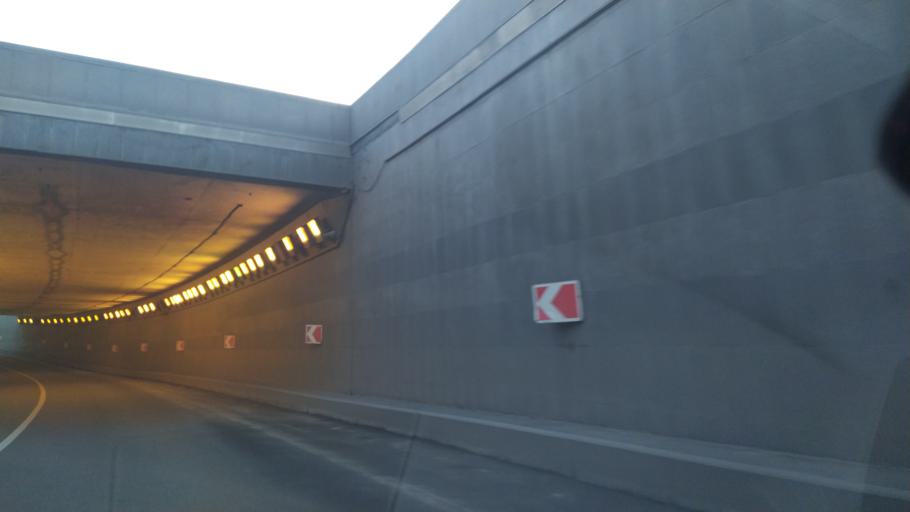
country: RU
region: St.-Petersburg
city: Aleksandrovskaya
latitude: 59.7781
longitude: 30.3254
